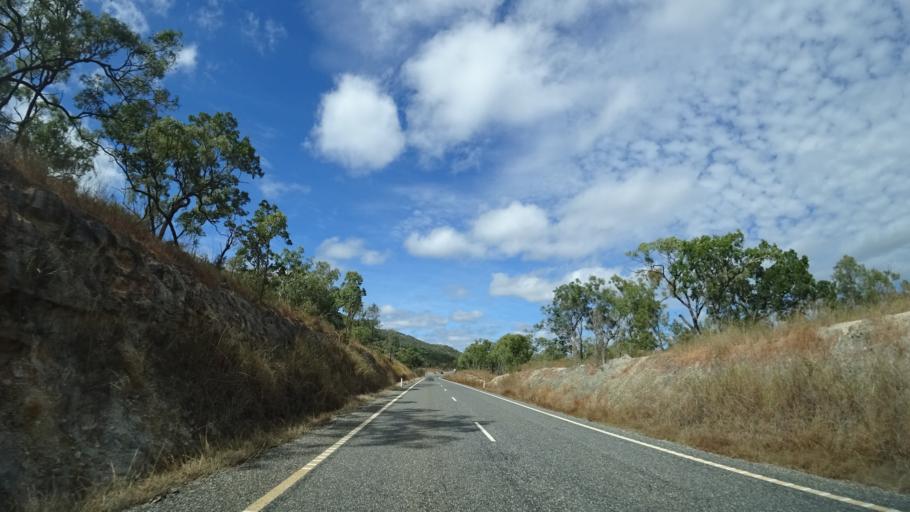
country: AU
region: Queensland
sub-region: Cairns
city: Port Douglas
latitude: -16.3358
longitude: 144.7239
